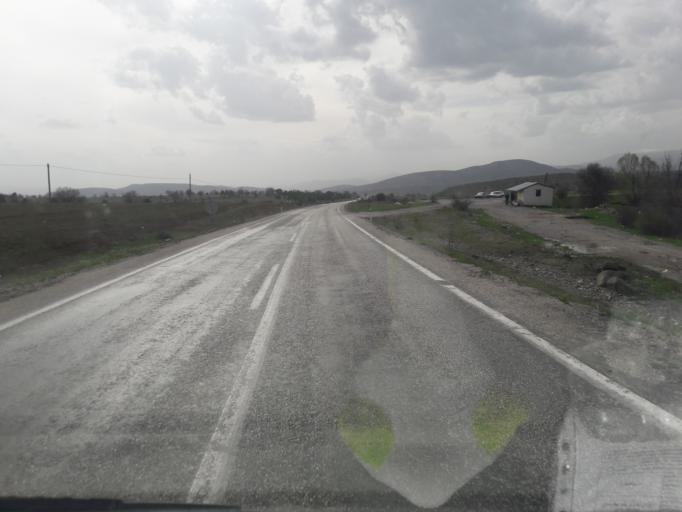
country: TR
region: Gumushane
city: Evren
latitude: 40.1698
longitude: 39.2536
